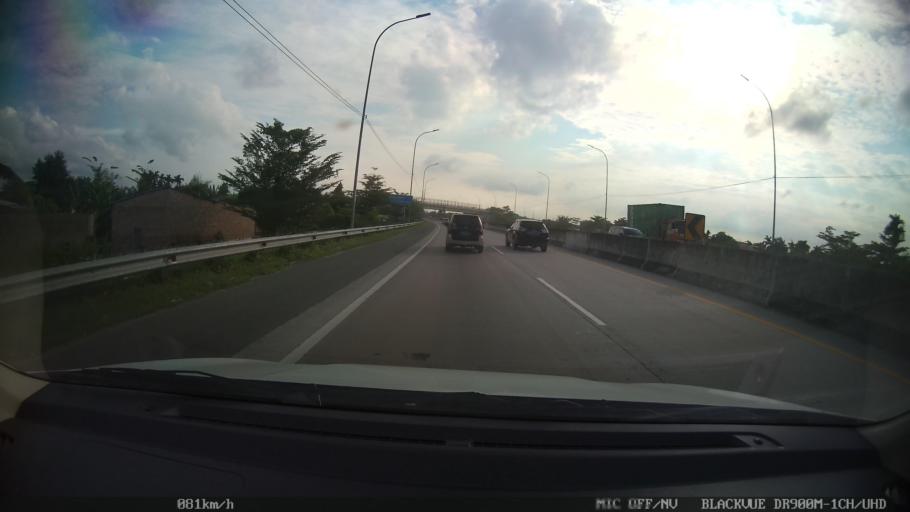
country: ID
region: North Sumatra
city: Medan
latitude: 3.6465
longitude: 98.6509
